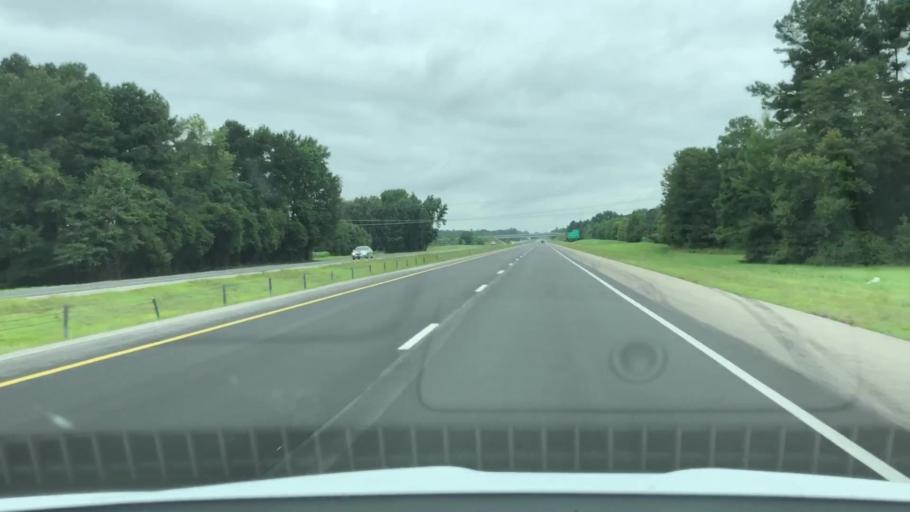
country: US
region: North Carolina
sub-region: Wayne County
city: Fremont
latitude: 35.5984
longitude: -77.9809
